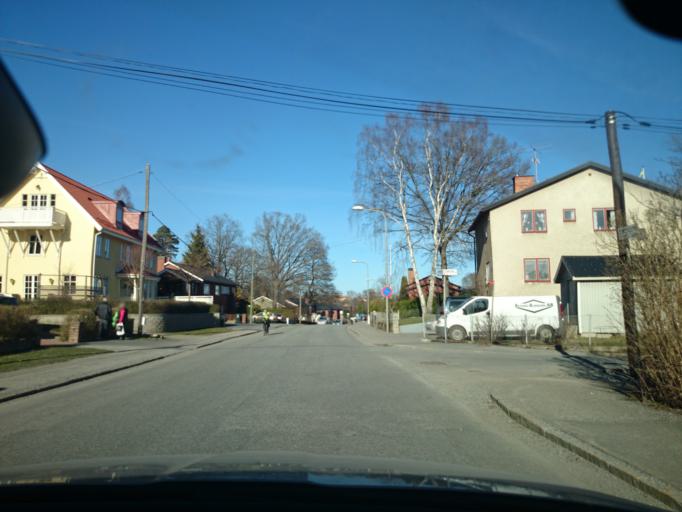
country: SE
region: Stockholm
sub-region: Huddinge Kommun
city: Segeltorp
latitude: 59.2791
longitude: 17.9588
